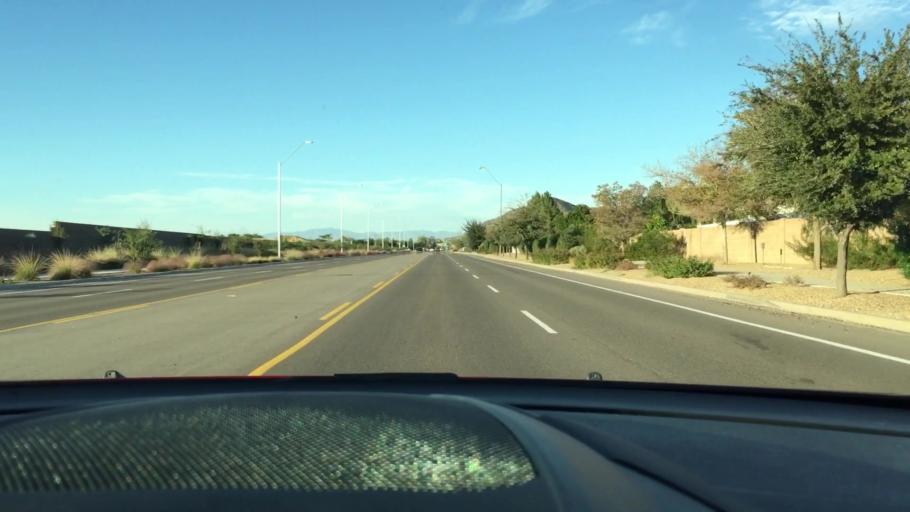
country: US
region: Arizona
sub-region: Maricopa County
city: Sun City West
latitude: 33.6916
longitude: -112.2551
